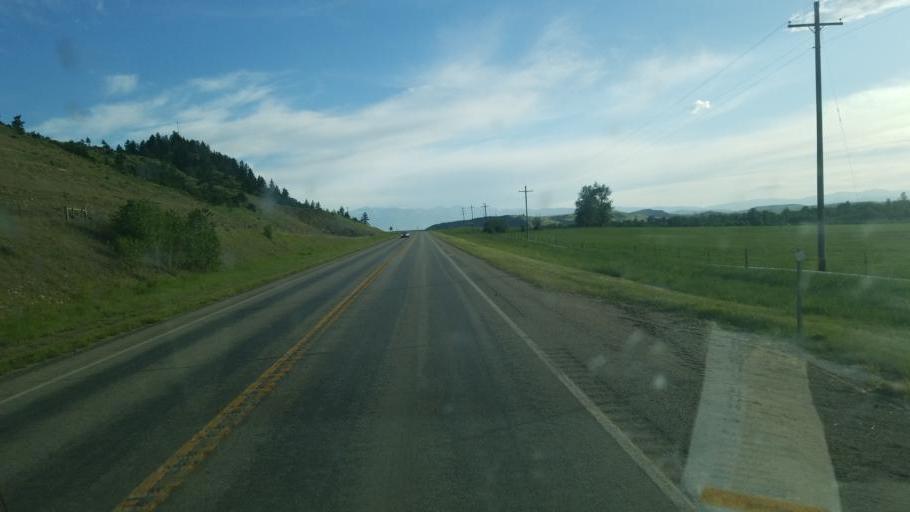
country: US
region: Montana
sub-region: Stillwater County
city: Absarokee
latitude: 45.5357
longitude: -109.4214
